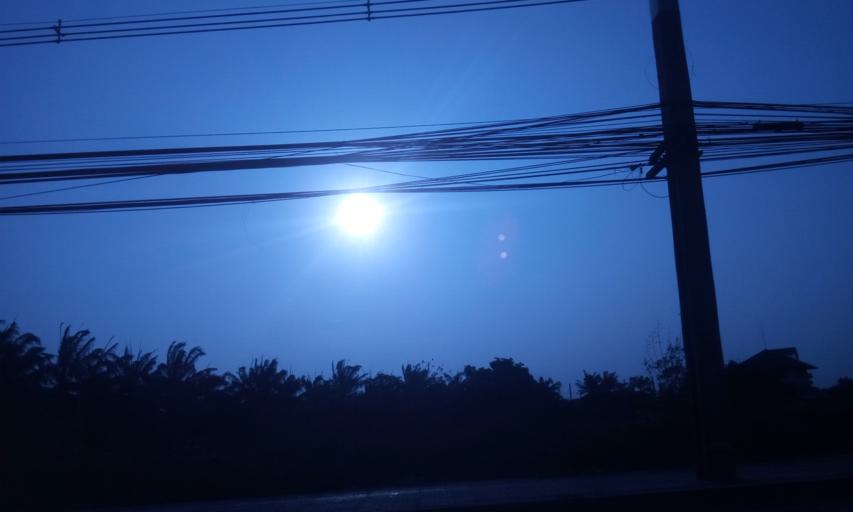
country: TH
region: Phra Nakhon Si Ayutthaya
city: Ban Bang Kadi Pathum Thani
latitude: 13.9777
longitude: 100.5506
